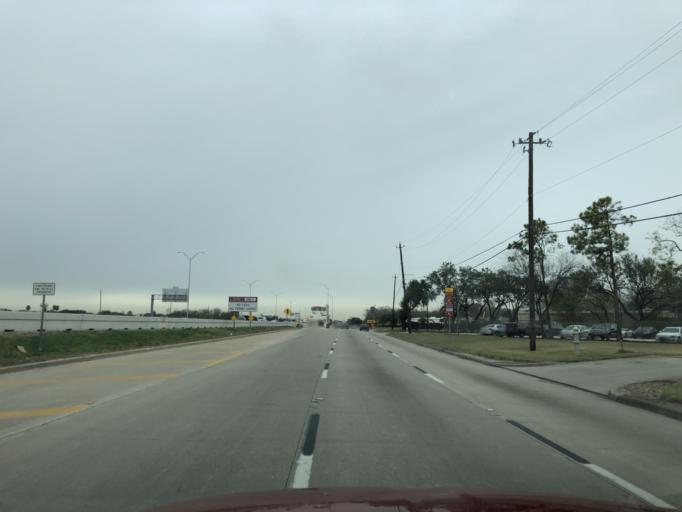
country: US
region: Texas
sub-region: Fort Bend County
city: Missouri City
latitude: 29.6318
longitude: -95.5239
